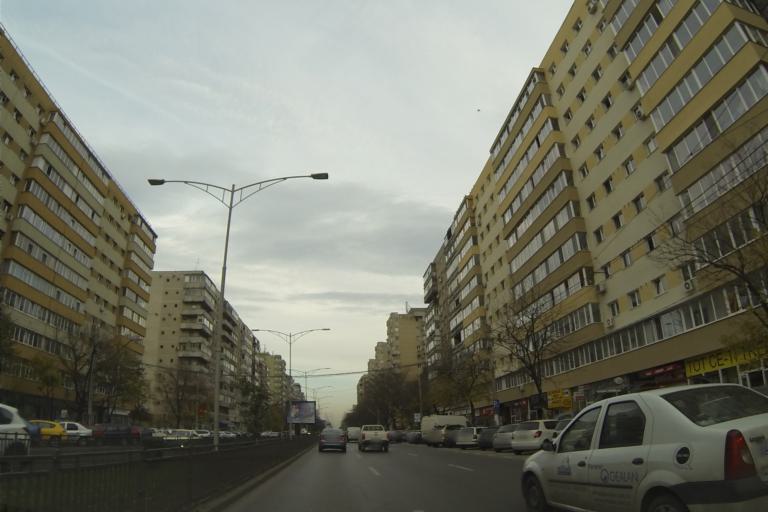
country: RO
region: Ilfov
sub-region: Comuna Chiajna
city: Rosu
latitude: 44.4338
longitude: 26.0091
